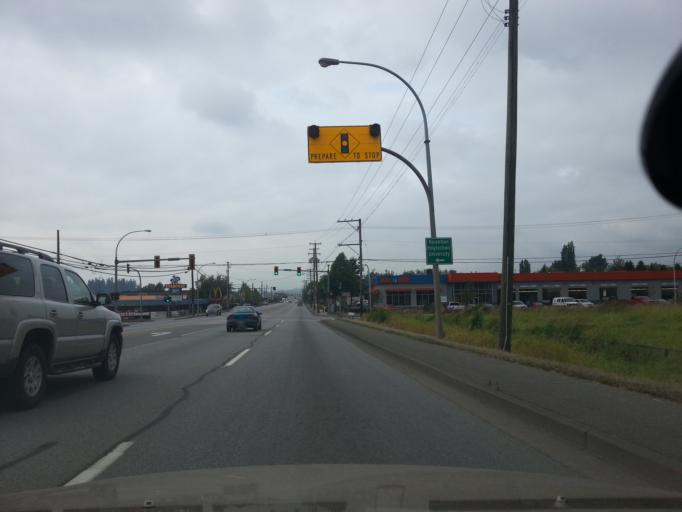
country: CA
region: British Columbia
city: Langley
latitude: 49.1042
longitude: -122.7227
